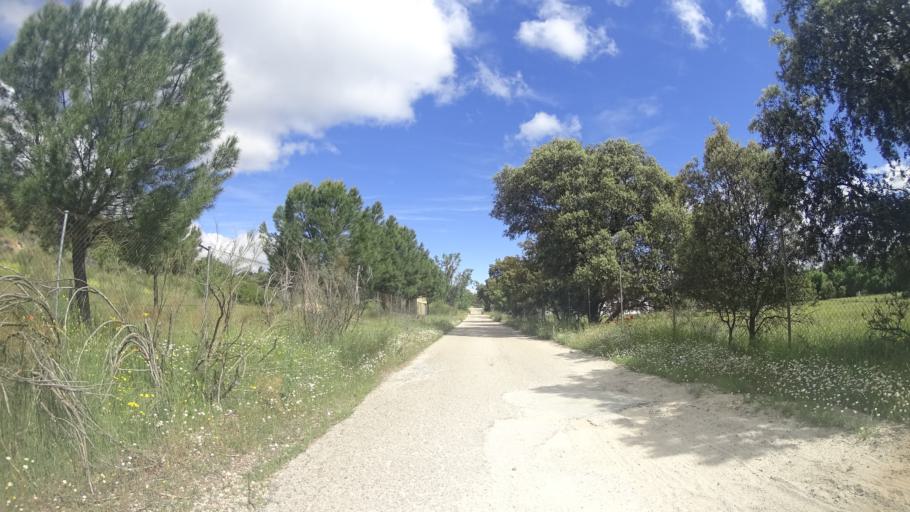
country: ES
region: Madrid
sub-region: Provincia de Madrid
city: Brunete
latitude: 40.4109
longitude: -3.9509
